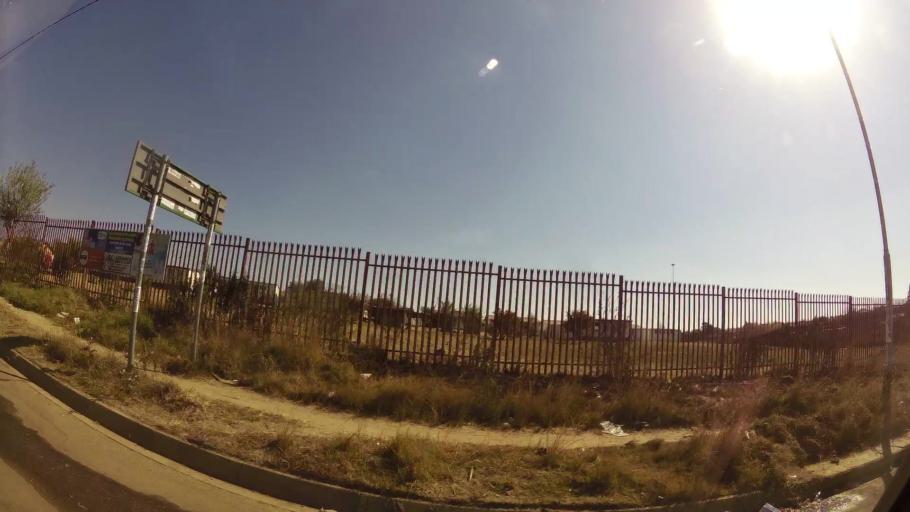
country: ZA
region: Gauteng
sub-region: City of Johannesburg Metropolitan Municipality
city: Midrand
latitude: -25.9150
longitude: 28.0962
